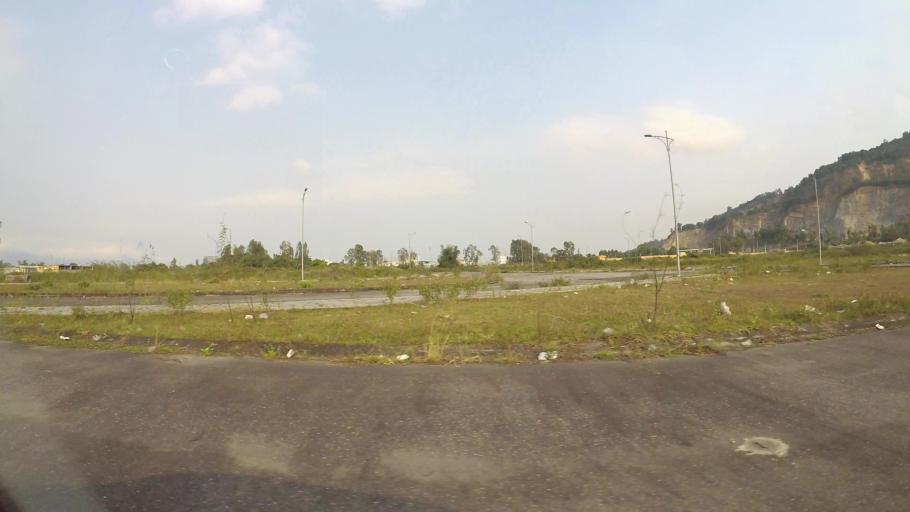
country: VN
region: Da Nang
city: Lien Chieu
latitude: 16.0465
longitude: 108.1603
